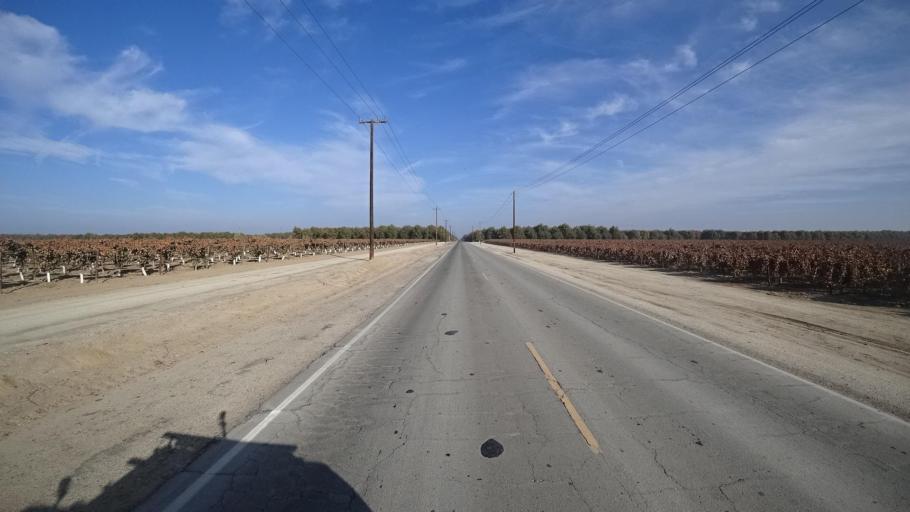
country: US
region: California
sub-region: Kern County
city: McFarland
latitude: 35.6146
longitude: -119.2042
